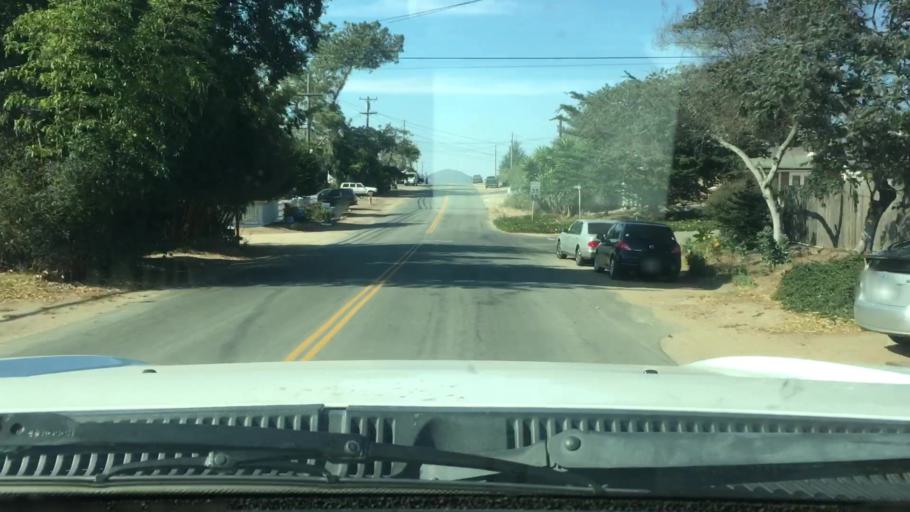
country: US
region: California
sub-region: San Luis Obispo County
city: Los Osos
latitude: 35.3198
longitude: -120.8310
